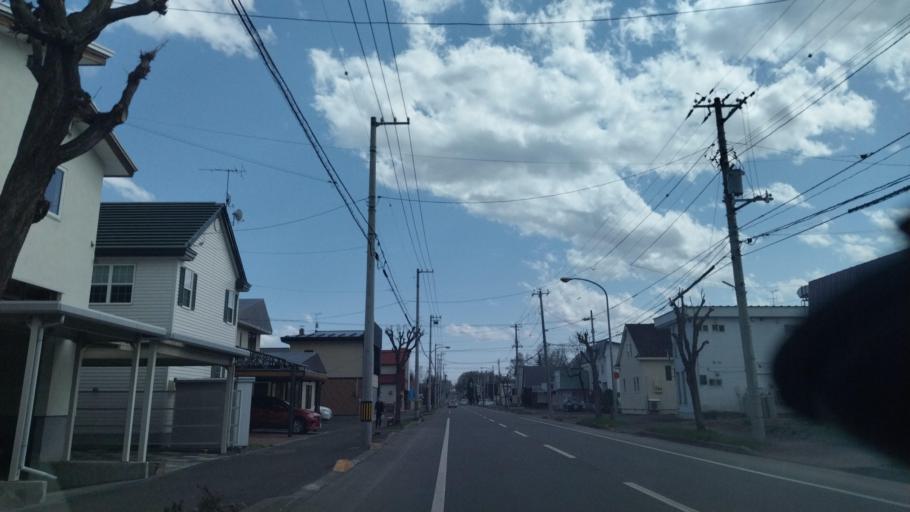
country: JP
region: Hokkaido
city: Obihiro
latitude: 42.9102
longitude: 143.1523
